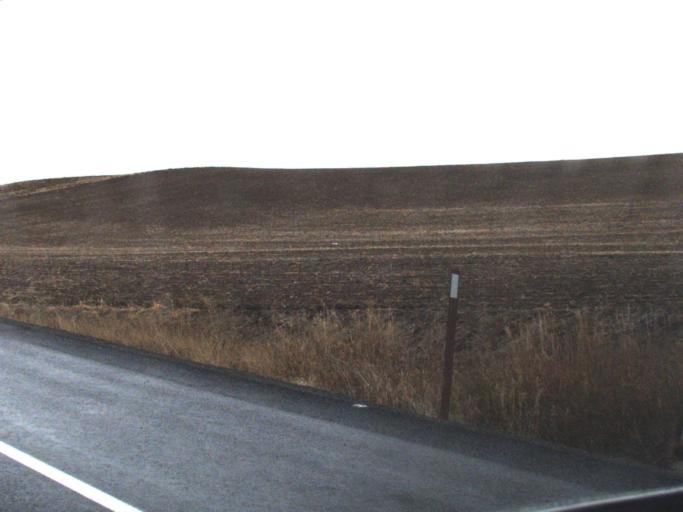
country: US
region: Washington
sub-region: Whitman County
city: Pullman
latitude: 46.7585
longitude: -117.2555
